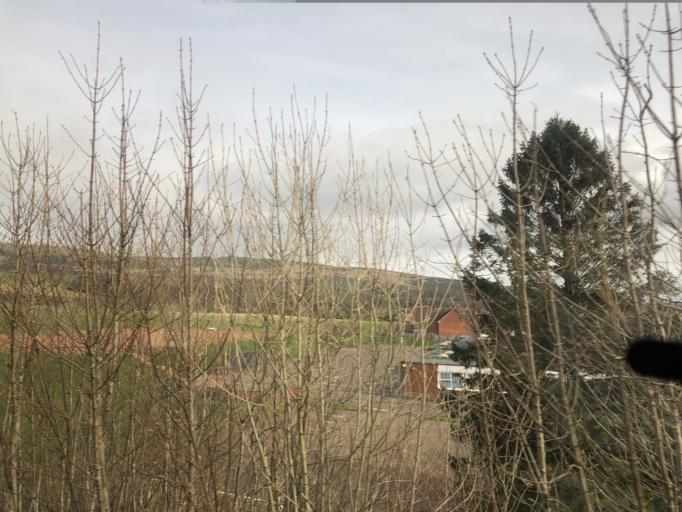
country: GB
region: Scotland
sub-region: Argyll and Bute
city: Helensburgh
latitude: 56.0011
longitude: -4.7108
